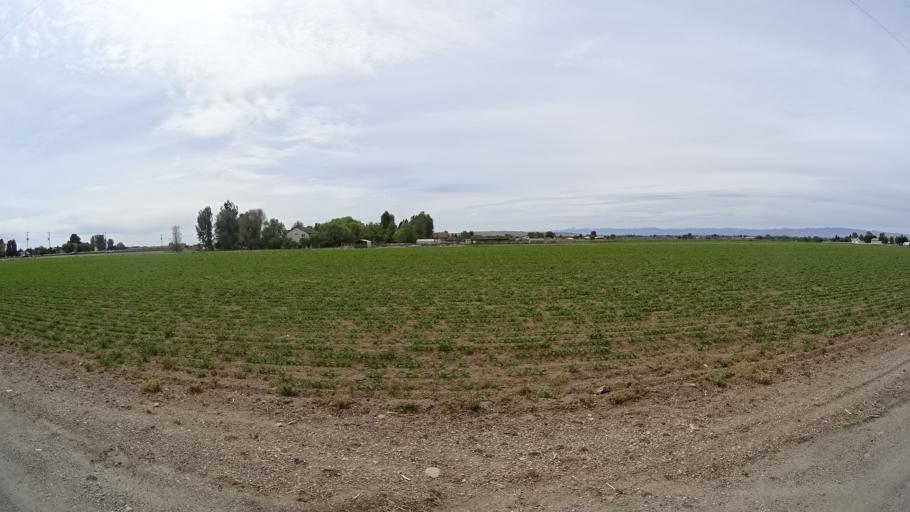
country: US
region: Idaho
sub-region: Ada County
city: Kuna
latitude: 43.5321
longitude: -116.4362
